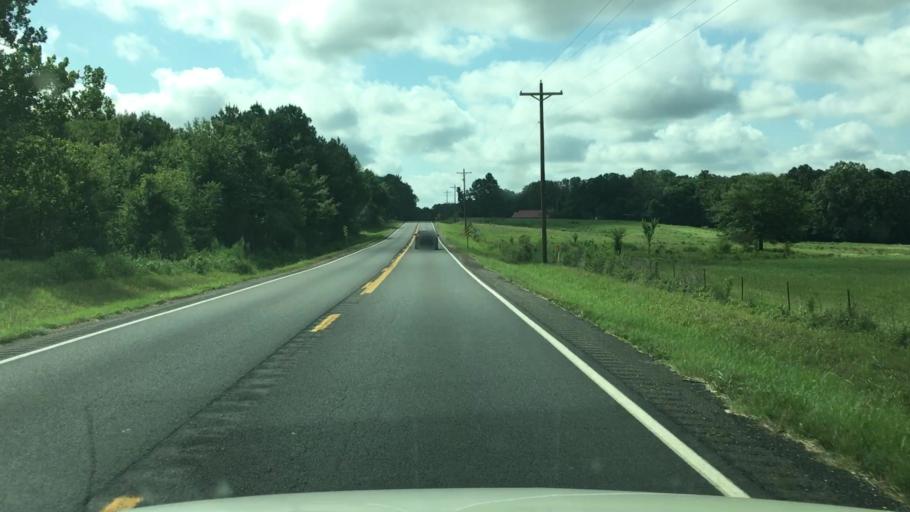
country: US
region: Arkansas
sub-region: Garland County
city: Lake Hamilton
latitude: 34.3345
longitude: -93.1779
